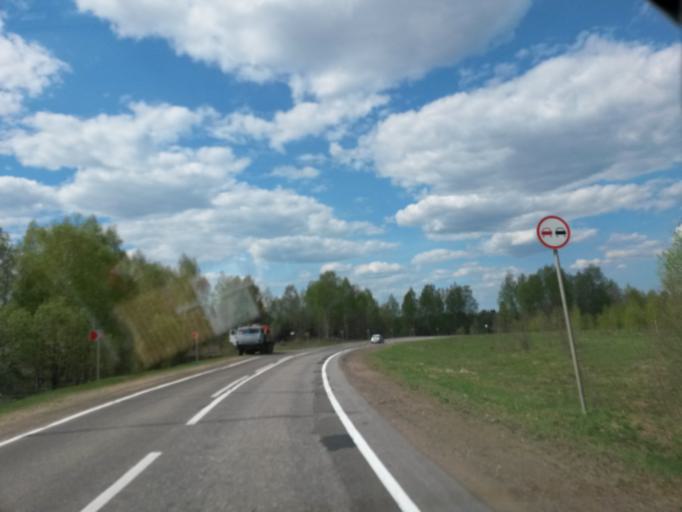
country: RU
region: Jaroslavl
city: Bol'shoye Selo
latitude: 57.6875
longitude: 39.1998
